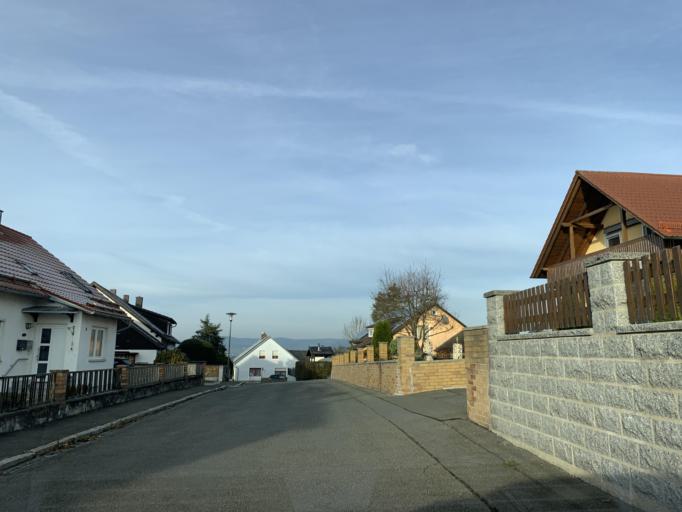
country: DE
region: Bavaria
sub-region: Upper Palatinate
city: Neunburg vorm Wald
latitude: 49.3501
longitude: 12.3944
